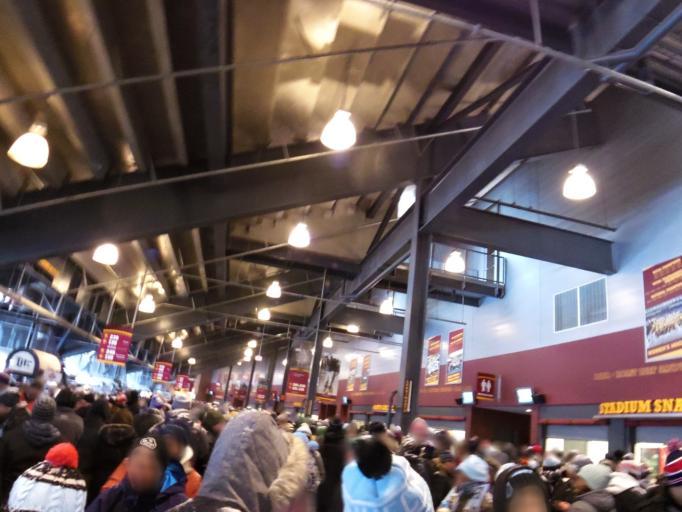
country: US
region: Minnesota
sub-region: Ramsey County
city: Lauderdale
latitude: 44.9775
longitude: -93.2246
